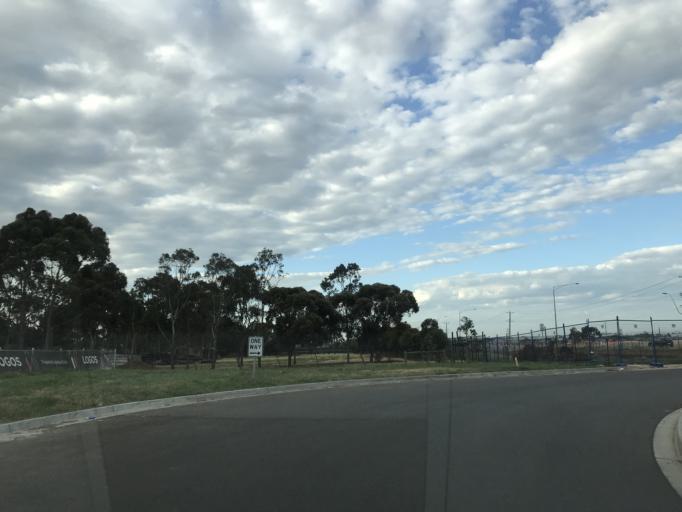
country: AU
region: Victoria
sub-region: Wyndham
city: Truganina
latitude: -37.8291
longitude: 144.7478
